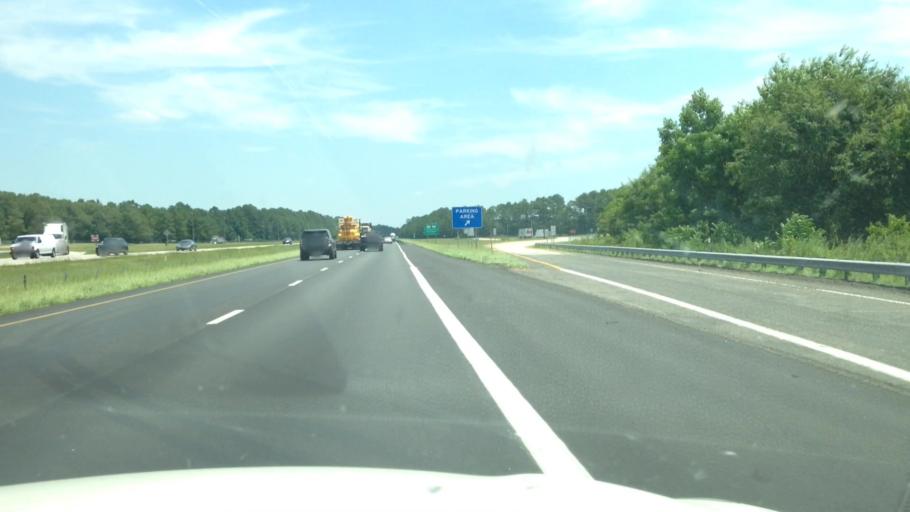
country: US
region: South Carolina
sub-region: Florence County
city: Timmonsville
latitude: 34.2033
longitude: -80.0589
